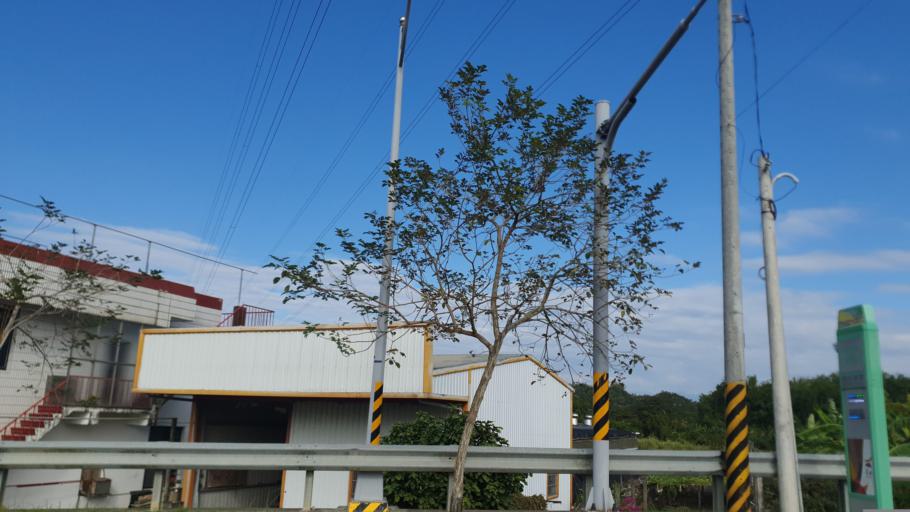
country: TW
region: Taiwan
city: Yujing
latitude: 23.0490
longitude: 120.4222
